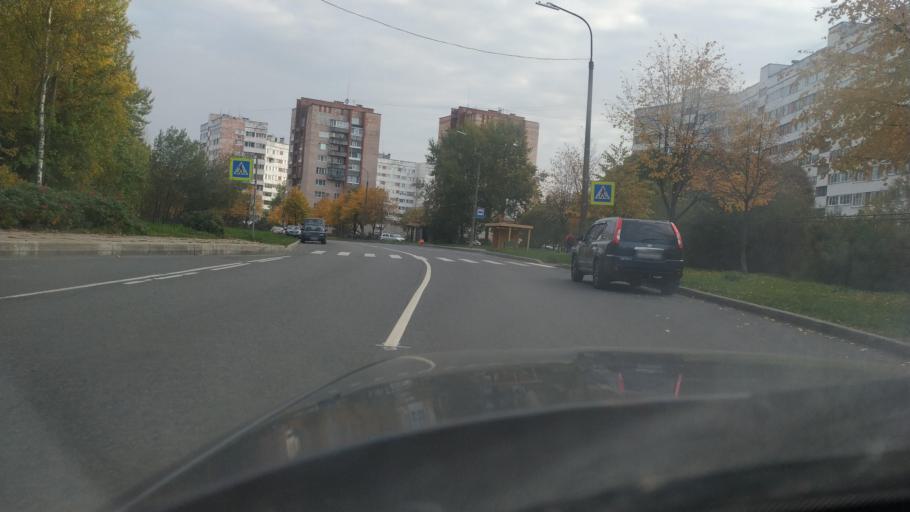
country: RU
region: Leningrad
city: Sosnovyy Bor
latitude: 59.9142
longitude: 29.0811
